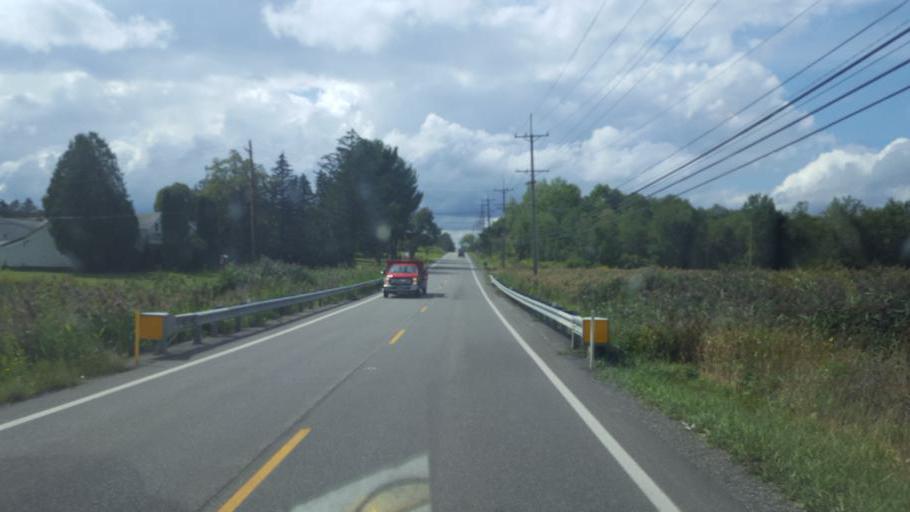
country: US
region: Ohio
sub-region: Geauga County
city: Middlefield
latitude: 41.4636
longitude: -81.1066
